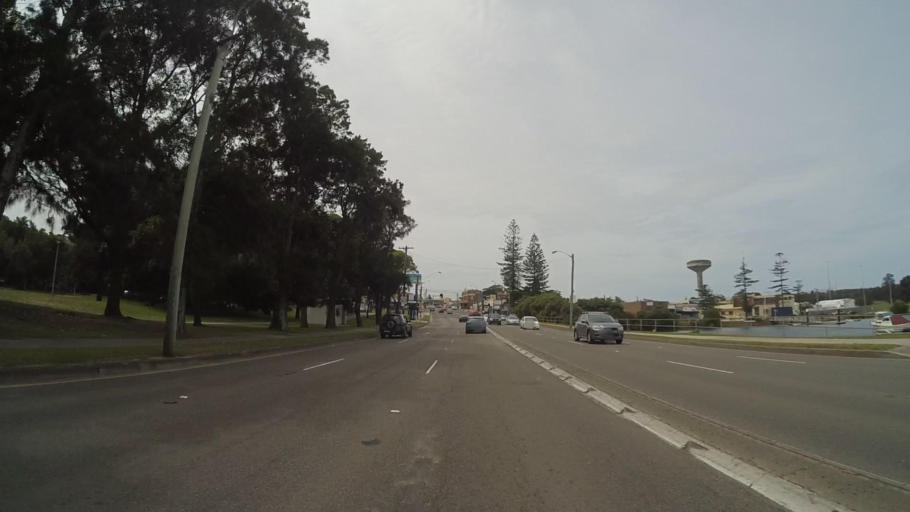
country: AU
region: New South Wales
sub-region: Rockdale
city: Arncliffe
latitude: -33.9279
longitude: 151.1578
